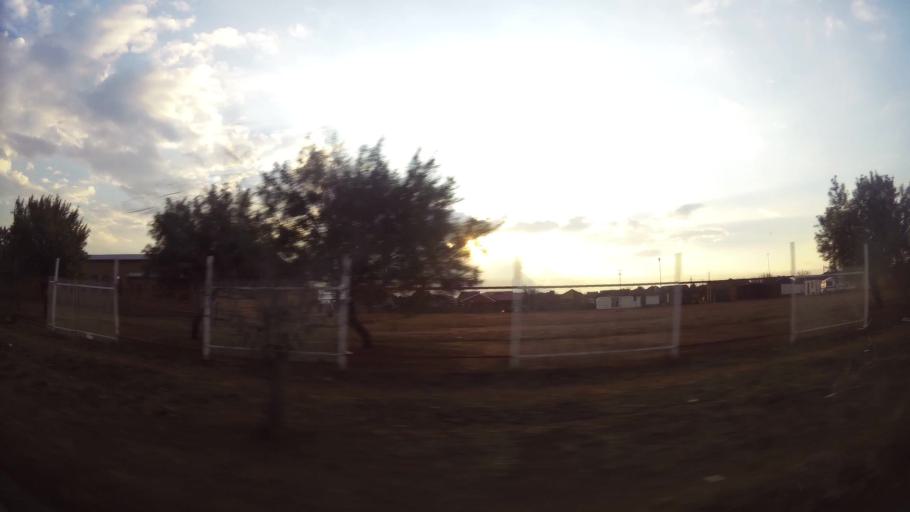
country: ZA
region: Gauteng
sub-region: City of Johannesburg Metropolitan Municipality
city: Orange Farm
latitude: -26.5673
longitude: 27.8618
